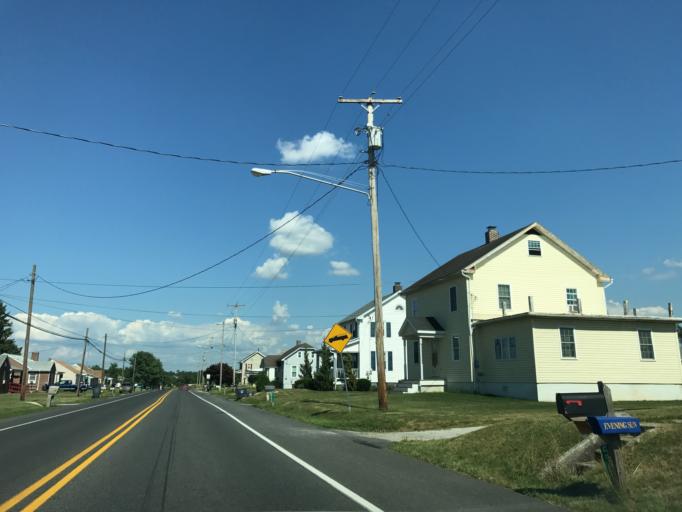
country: US
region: Pennsylvania
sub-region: Adams County
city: McSherrystown
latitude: 39.7970
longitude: -77.0382
